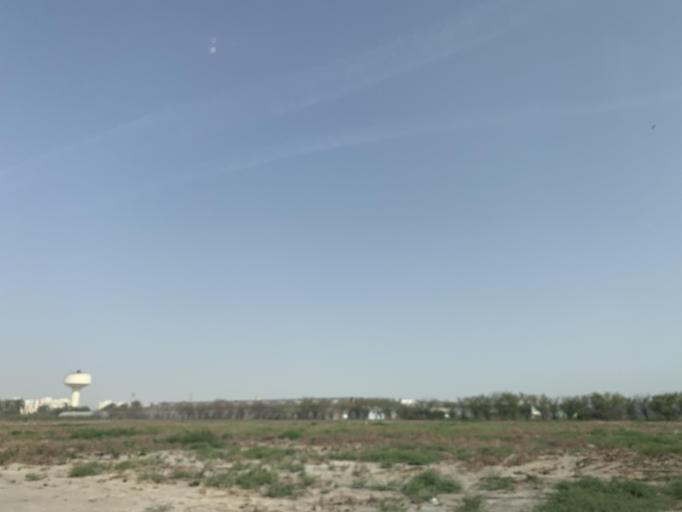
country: BH
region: Northern
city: Madinat `Isa
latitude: 26.1685
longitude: 50.5291
